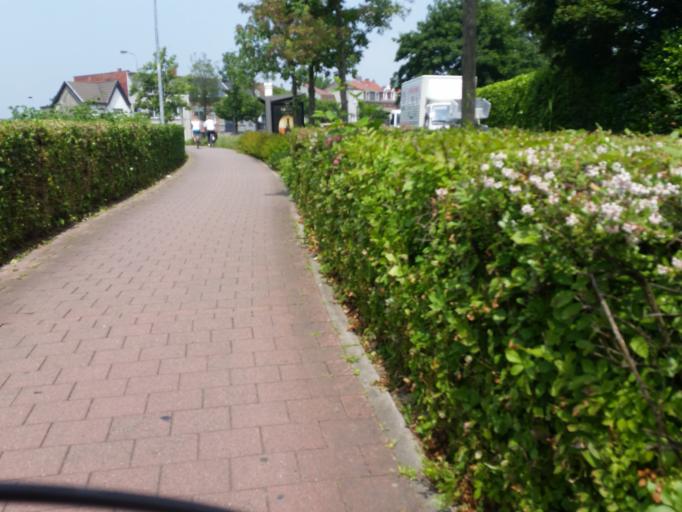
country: BE
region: Flanders
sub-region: Provincie Antwerpen
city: Mortsel
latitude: 51.1815
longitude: 4.4482
